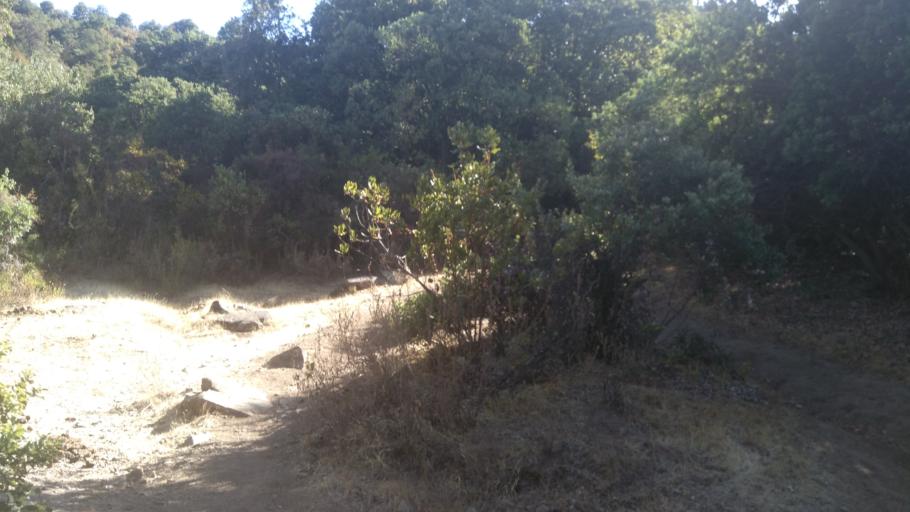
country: CL
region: Santiago Metropolitan
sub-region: Provincia de Cordillera
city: Puente Alto
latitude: -33.7186
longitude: -70.4626
